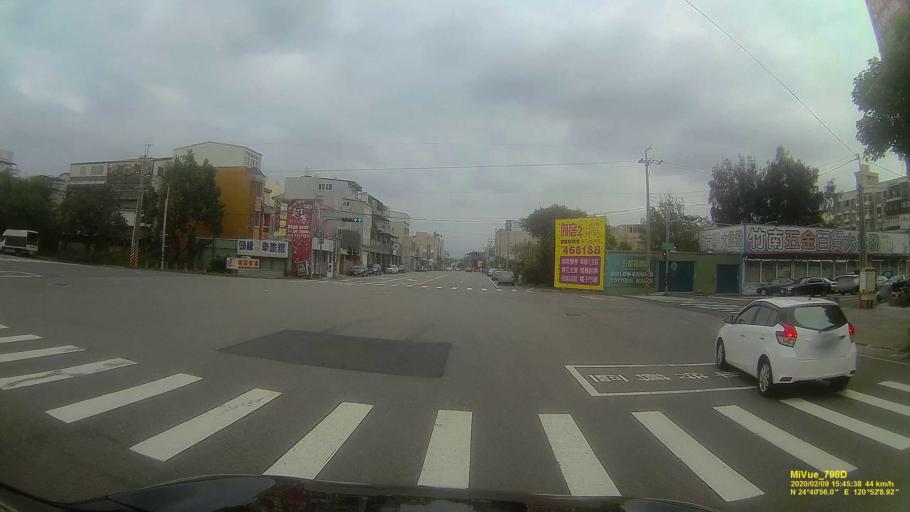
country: TW
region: Taiwan
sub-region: Miaoli
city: Miaoli
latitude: 24.6820
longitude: 120.8692
